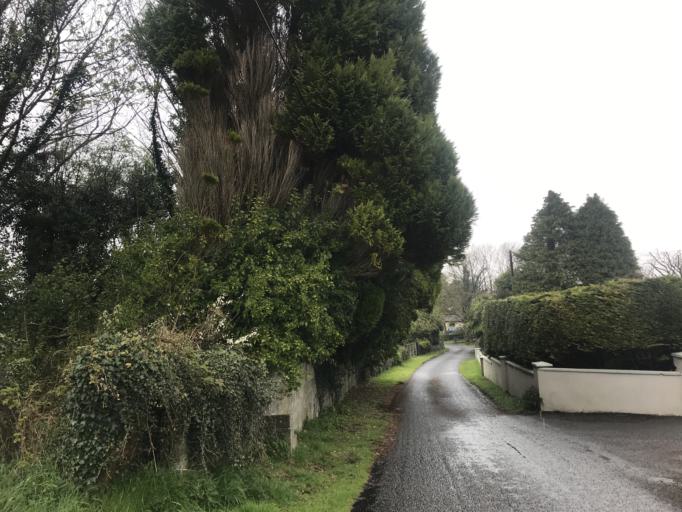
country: IE
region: Connaught
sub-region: County Galway
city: Gaillimh
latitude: 53.2954
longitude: -9.0104
